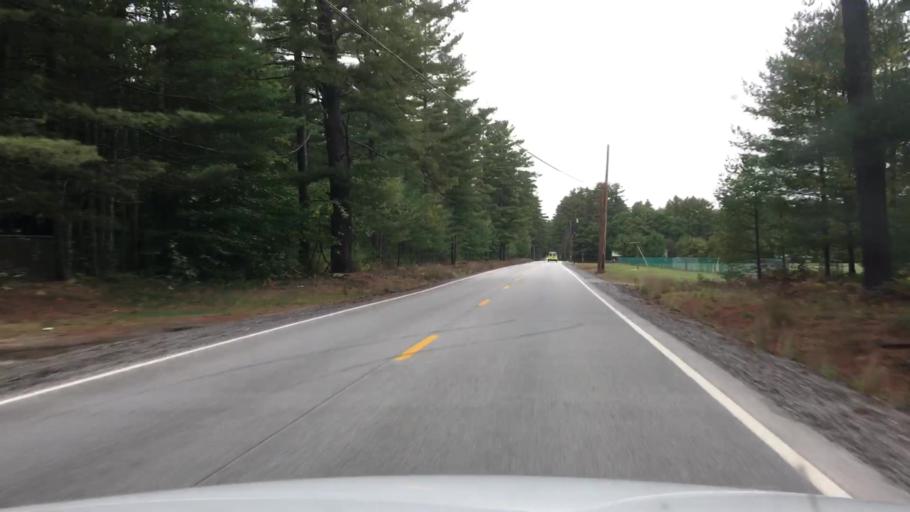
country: US
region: Maine
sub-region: Cumberland County
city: Harrison
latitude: 44.2248
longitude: -70.6982
